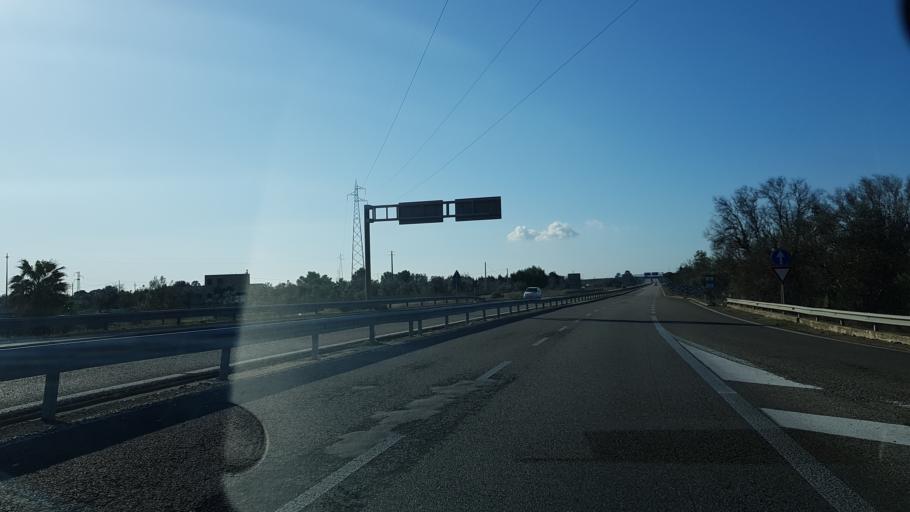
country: IT
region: Apulia
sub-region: Provincia di Lecce
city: Galatone
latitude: 40.1248
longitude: 18.0518
